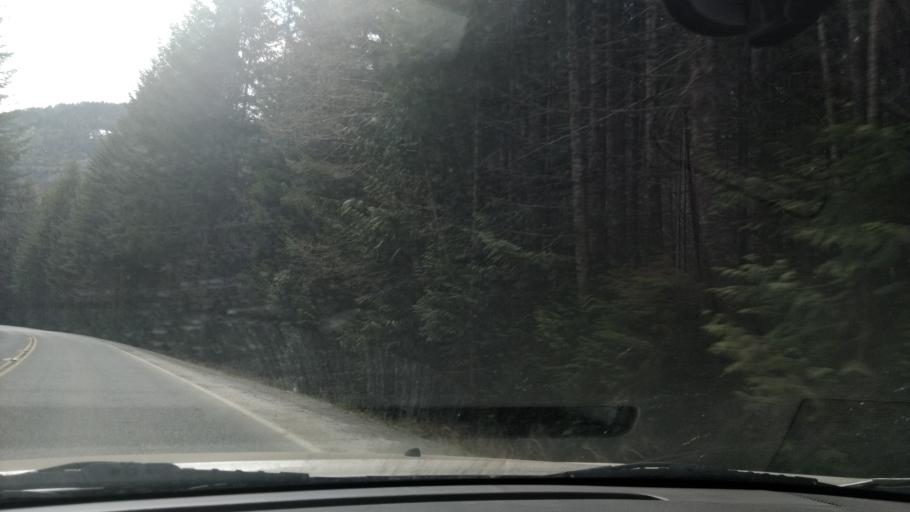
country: CA
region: British Columbia
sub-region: Regional District of Alberni-Clayoquot
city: Tofino
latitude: 49.8249
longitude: -125.9747
